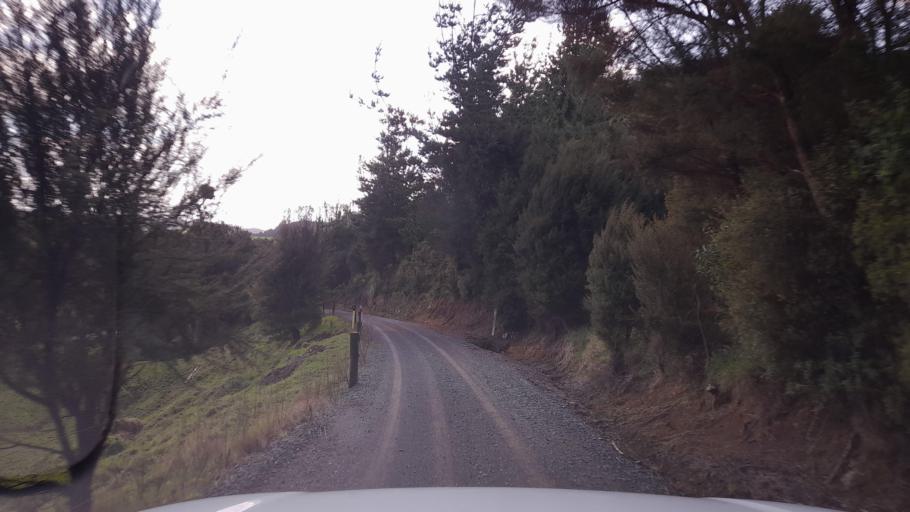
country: NZ
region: Northland
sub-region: Far North District
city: Waimate North
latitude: -35.1585
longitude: 173.7124
